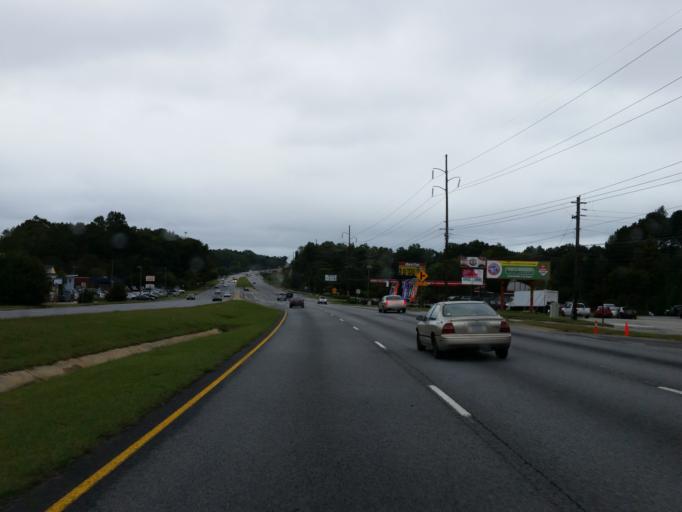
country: US
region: Georgia
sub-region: Clayton County
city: Jonesboro
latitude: 33.5460
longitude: -84.3692
